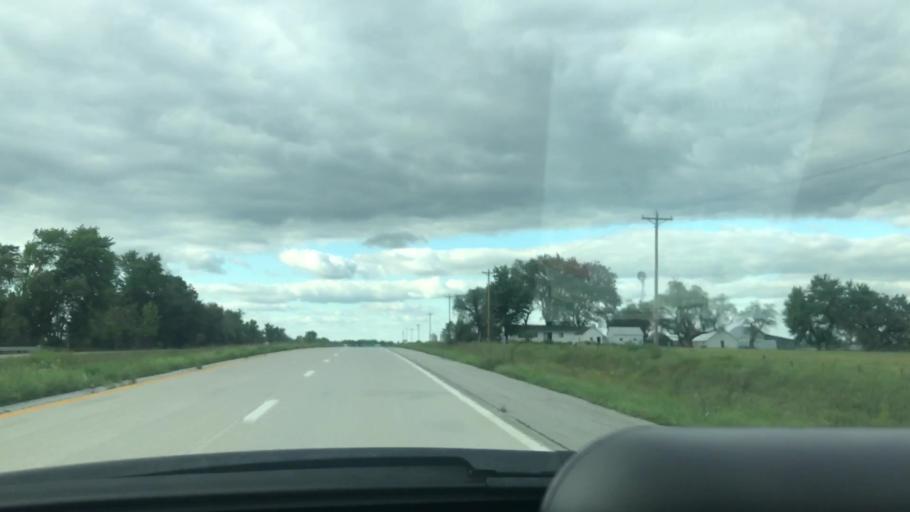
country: US
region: Missouri
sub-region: Benton County
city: Lincoln
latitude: 38.3678
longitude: -93.3388
